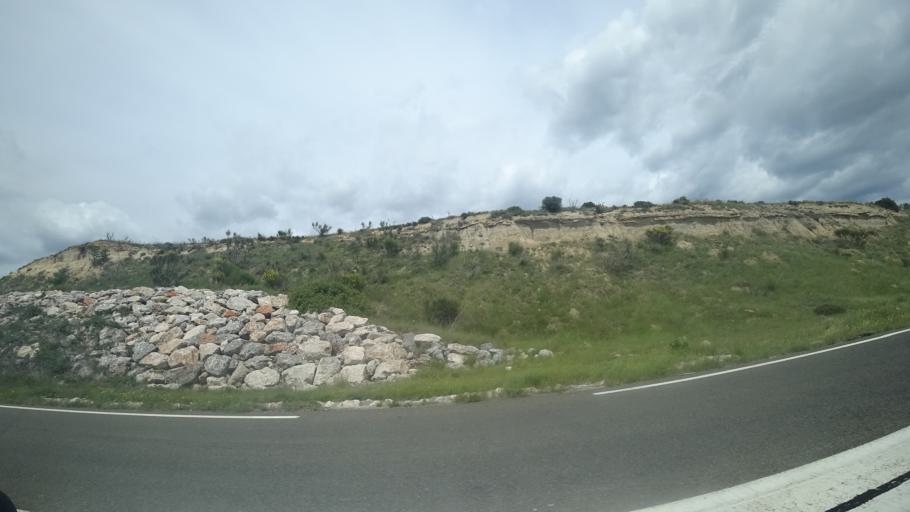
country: FR
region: Languedoc-Roussillon
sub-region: Departement de l'Aude
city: Leucate
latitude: 42.9295
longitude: 3.0166
